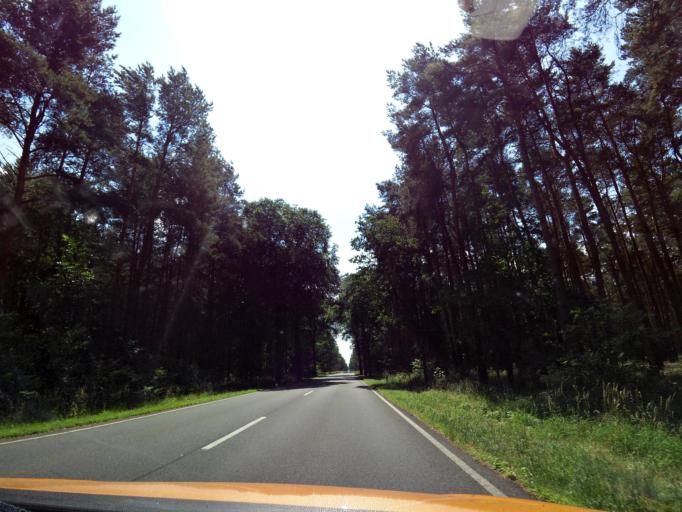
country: DE
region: Brandenburg
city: Friesack
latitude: 52.8031
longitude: 12.5458
